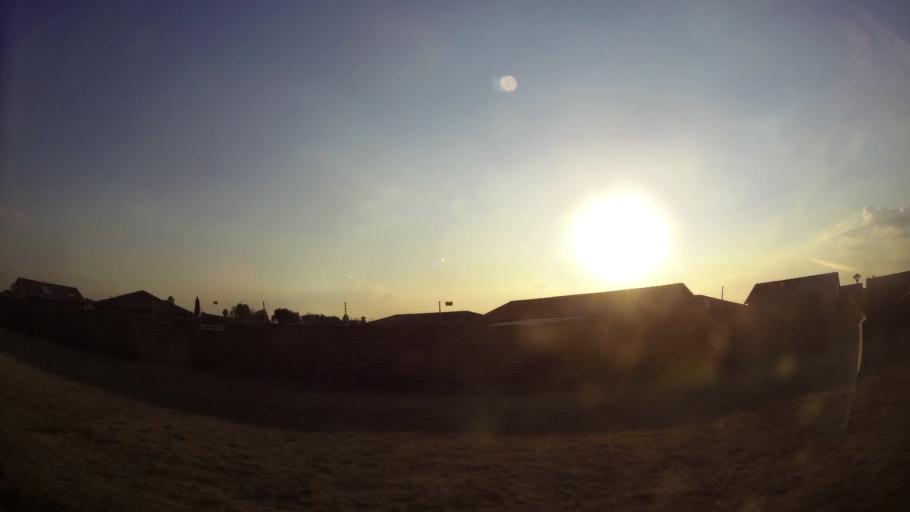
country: ZA
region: Gauteng
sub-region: Ekurhuleni Metropolitan Municipality
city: Boksburg
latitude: -26.3028
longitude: 28.2492
